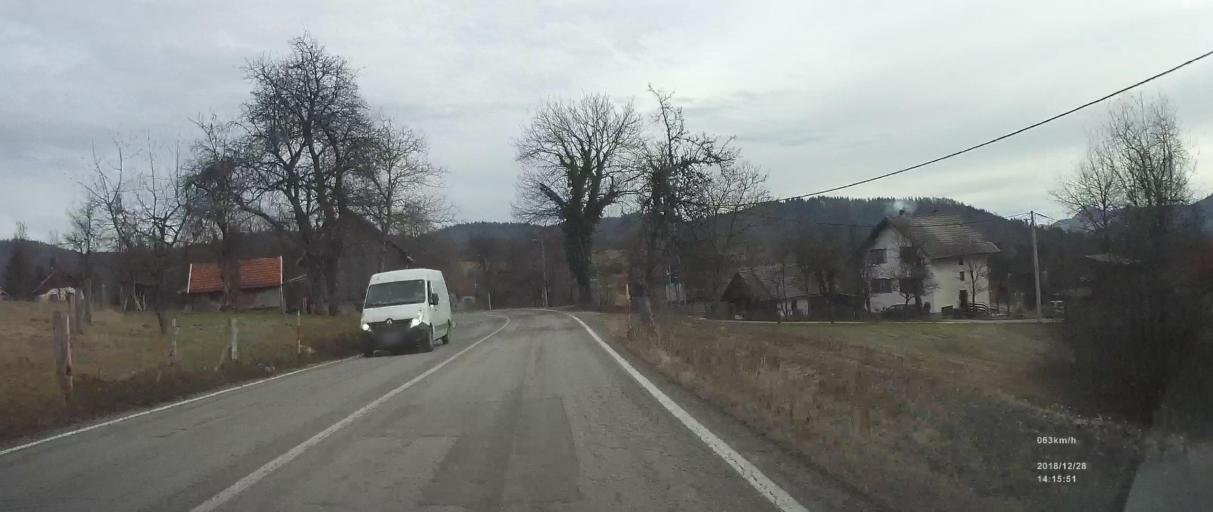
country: HR
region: Primorsko-Goranska
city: Vrbovsko
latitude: 45.4219
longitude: 15.0303
